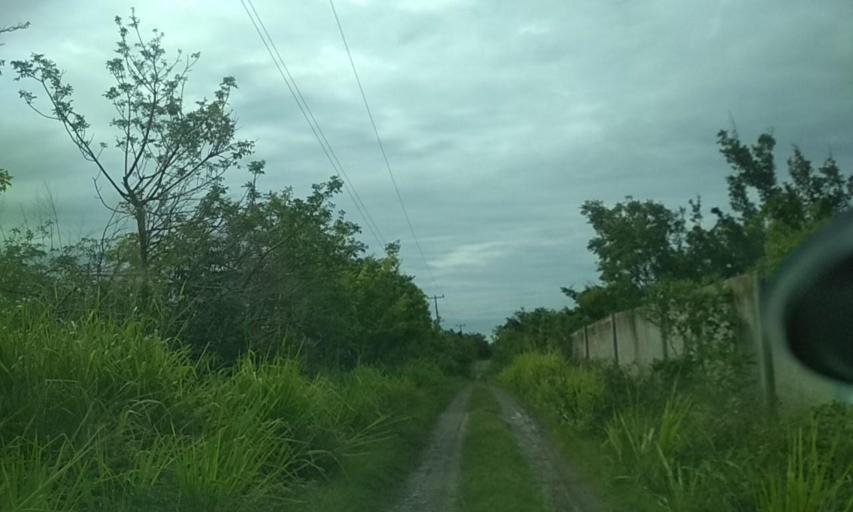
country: MX
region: Veracruz
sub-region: Cazones de Herrera
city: Rancho Nuevo
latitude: 20.6043
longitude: -97.1409
